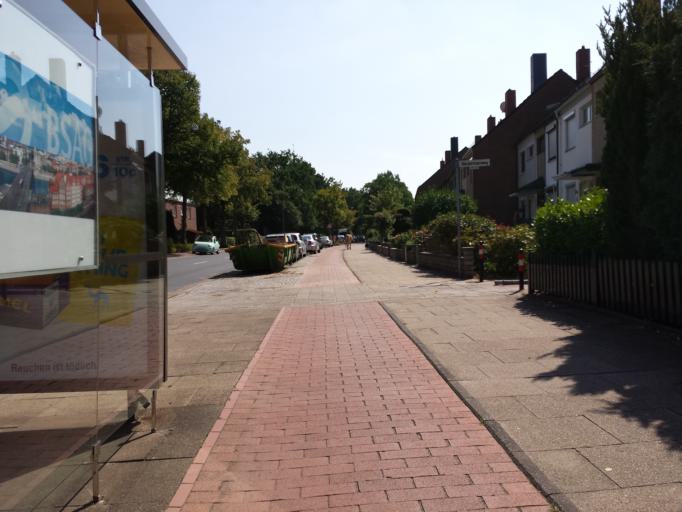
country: DE
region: Bremen
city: Bremen
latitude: 53.0333
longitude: 8.8511
